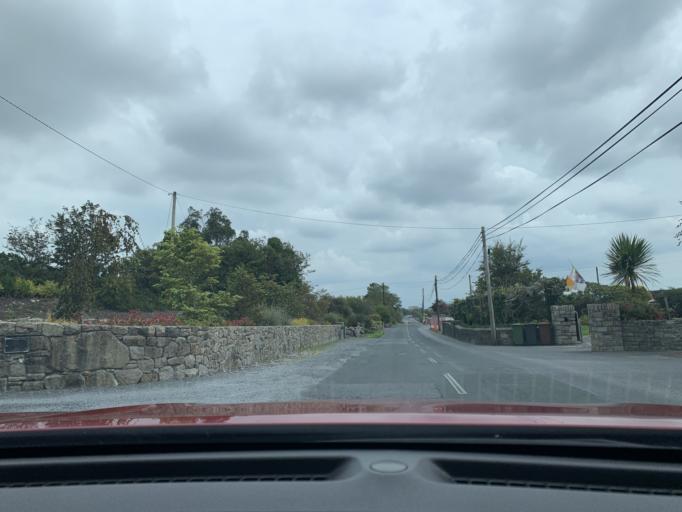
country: IE
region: Connaught
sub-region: County Galway
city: Gaillimh
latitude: 53.2781
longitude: -9.1017
